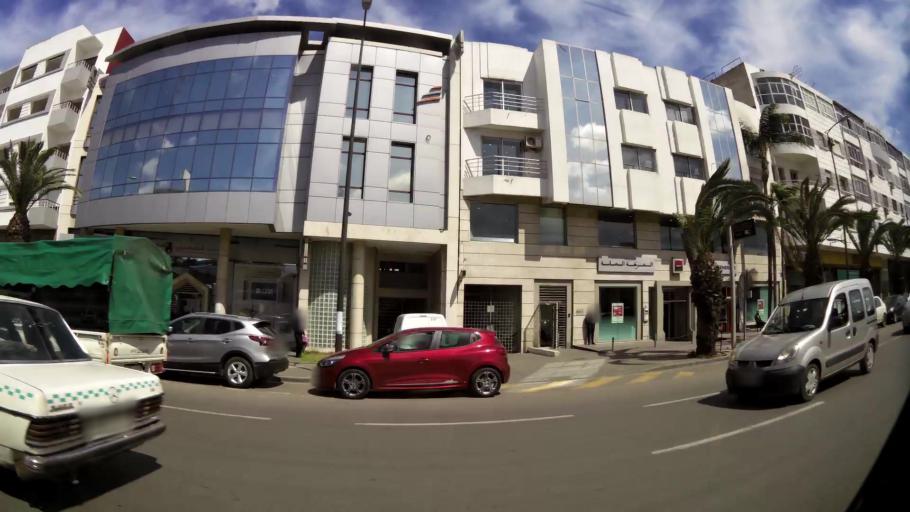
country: MA
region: Grand Casablanca
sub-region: Mediouna
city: Tit Mellil
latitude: 33.6047
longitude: -7.5398
